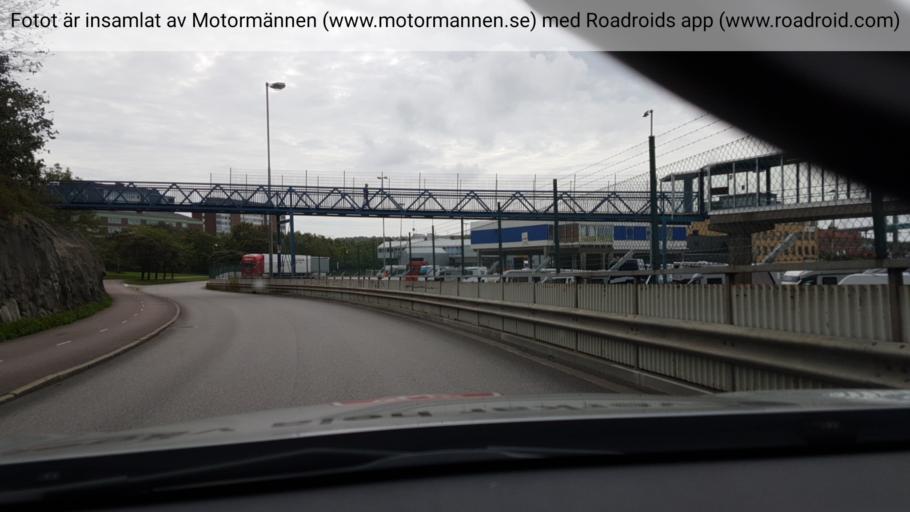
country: SE
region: Vaestra Goetaland
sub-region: Goteborg
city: Majorna
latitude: 57.6951
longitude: 11.9162
